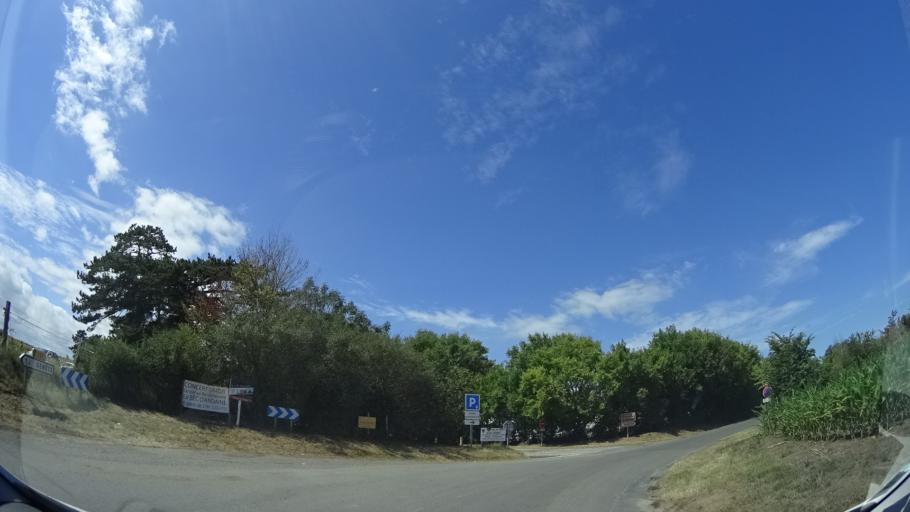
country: FR
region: Lower Normandy
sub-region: Departement de la Manche
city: Sartilly
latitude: 48.6875
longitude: -1.4962
